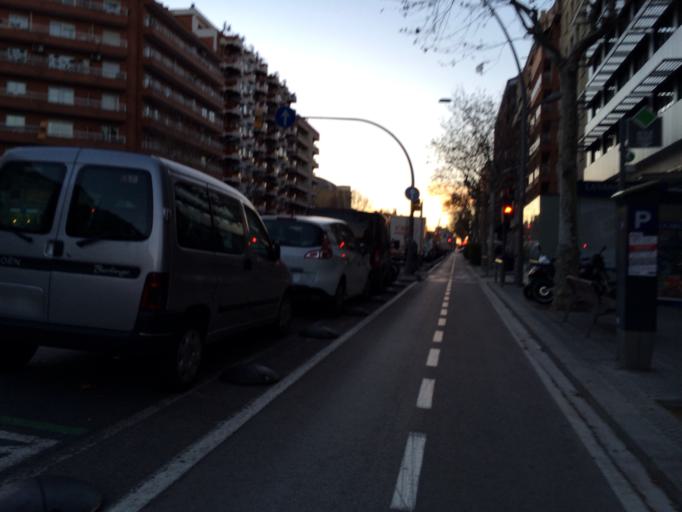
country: ES
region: Catalonia
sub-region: Provincia de Barcelona
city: Sants-Montjuic
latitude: 41.3750
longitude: 2.1561
